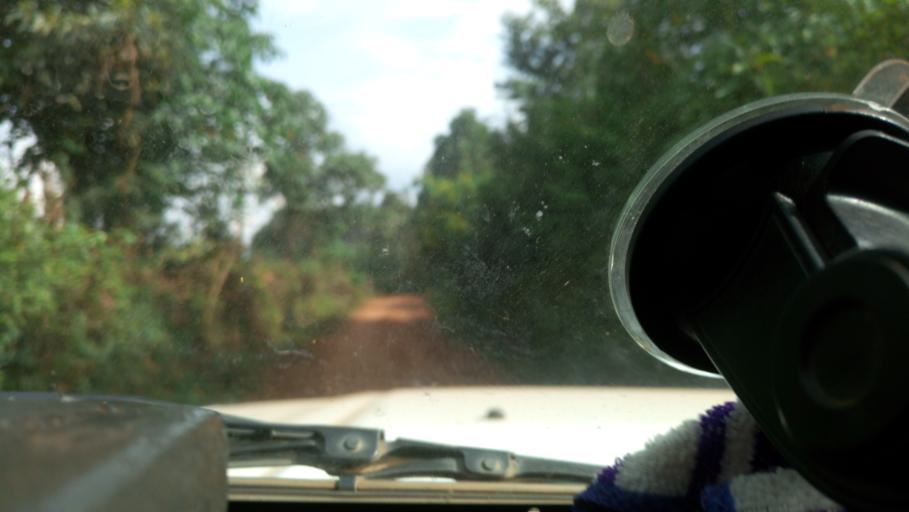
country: KE
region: Kericho
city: Litein
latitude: -0.5958
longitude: 35.1140
